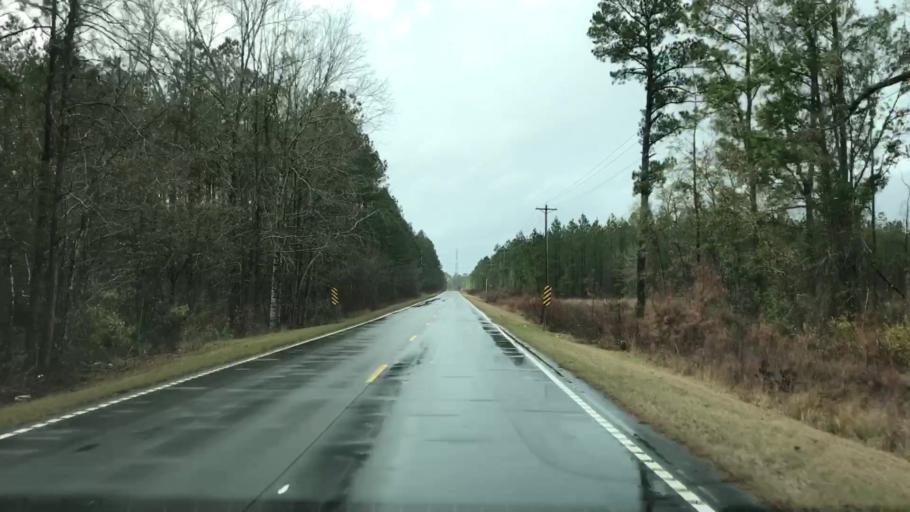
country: US
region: South Carolina
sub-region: Florence County
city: Johnsonville
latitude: 33.6761
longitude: -79.3396
